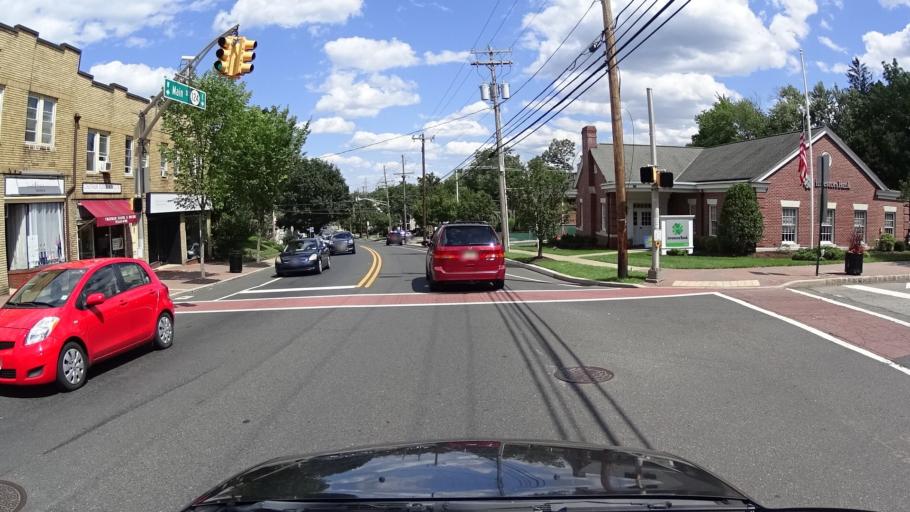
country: US
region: New Jersey
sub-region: Morris County
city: Chatham
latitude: 40.7397
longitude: -74.3796
